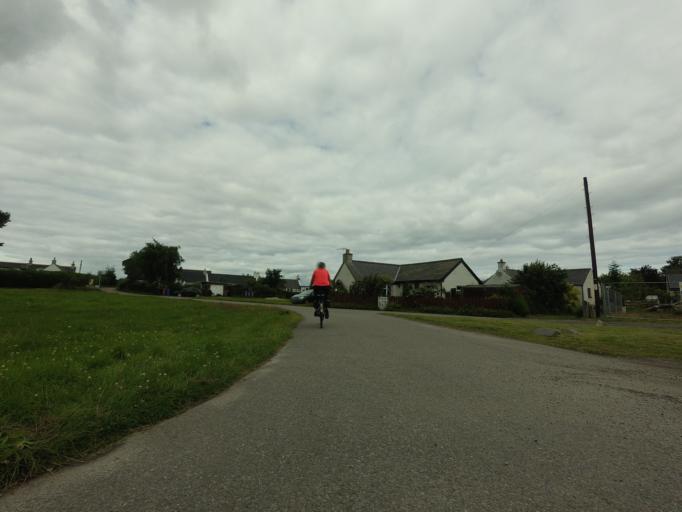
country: GB
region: Scotland
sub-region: Moray
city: Forres
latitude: 57.6126
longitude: -3.6425
